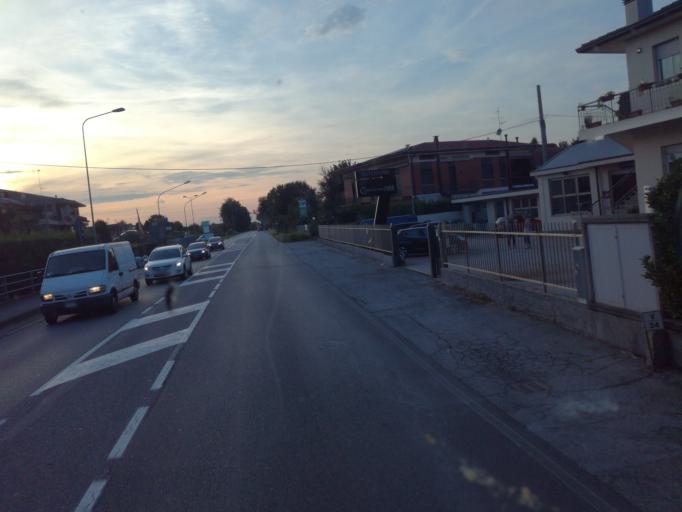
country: IT
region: Lombardy
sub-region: Provincia di Lecco
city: Barzago
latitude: 45.7541
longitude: 9.3135
